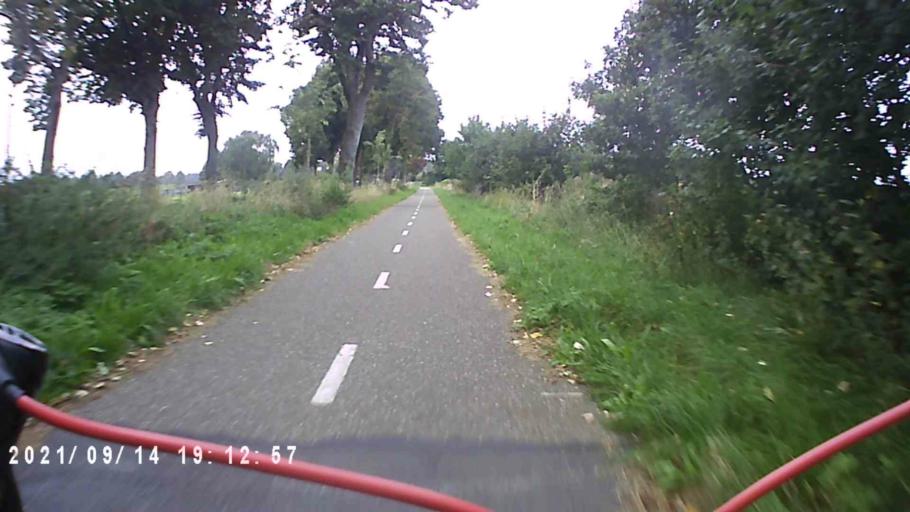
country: NL
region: Drenthe
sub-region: Gemeente Aa en Hunze
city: Anloo
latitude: 53.0645
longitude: 6.7108
